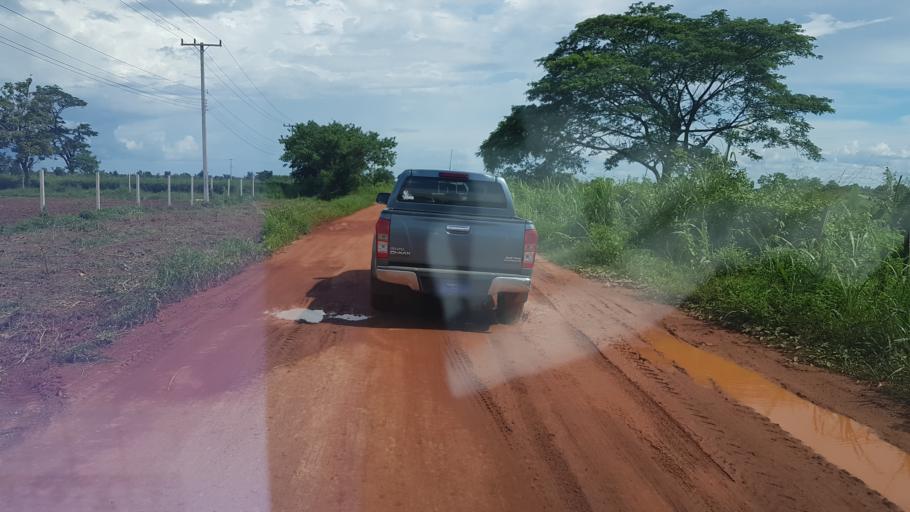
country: LA
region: Vientiane
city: Vientiane
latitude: 18.2212
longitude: 102.5689
